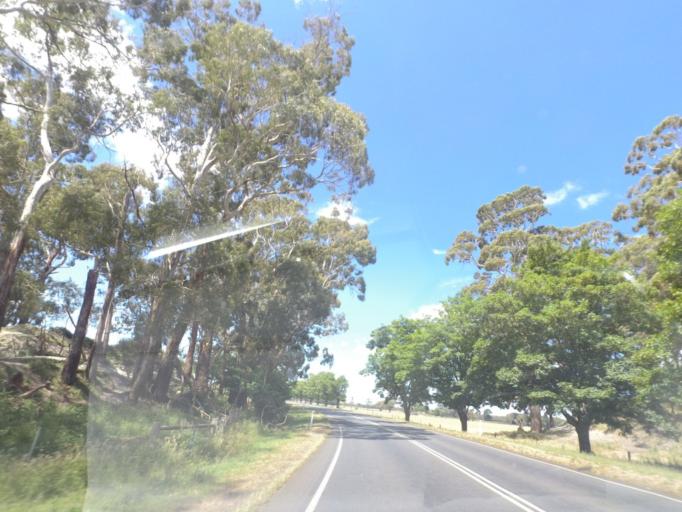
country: AU
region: Victoria
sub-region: Mount Alexander
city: Castlemaine
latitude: -37.3351
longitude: 144.1681
